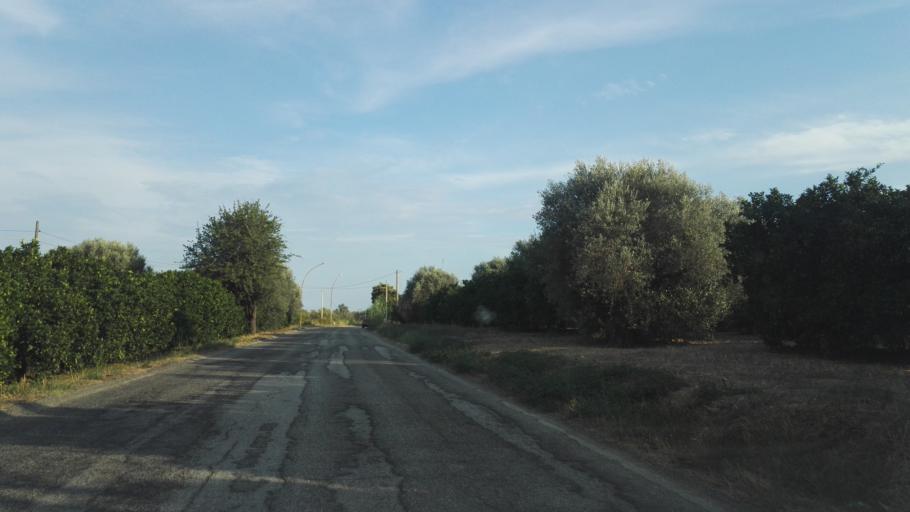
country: IT
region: Calabria
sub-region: Provincia di Reggio Calabria
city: Caulonia Marina
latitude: 38.3726
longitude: 16.4835
